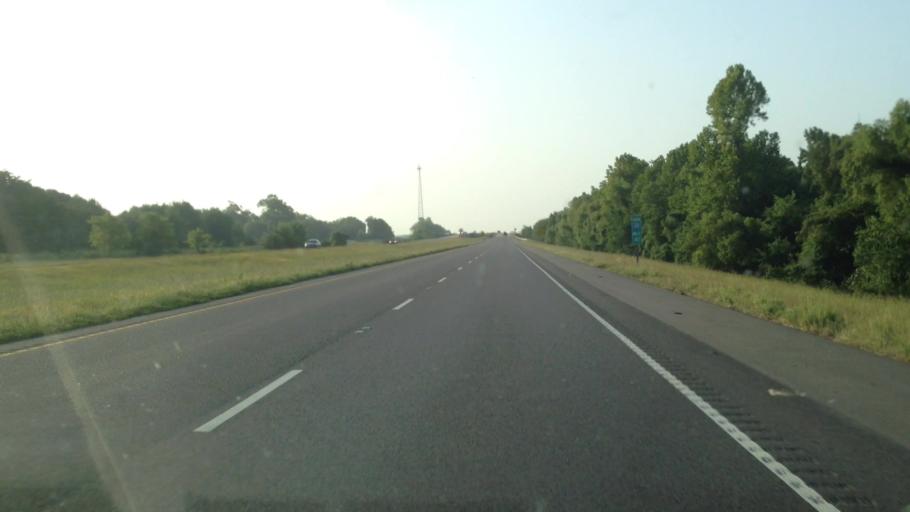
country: US
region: Louisiana
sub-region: Rapides Parish
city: Boyce
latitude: 31.3974
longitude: -92.7001
